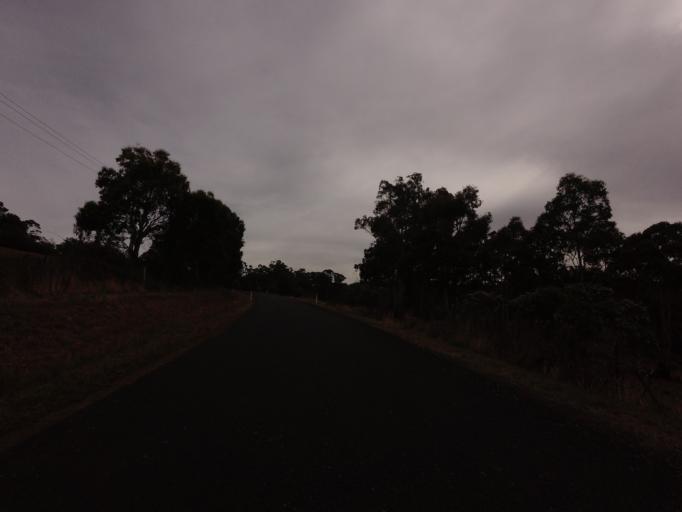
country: AU
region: Tasmania
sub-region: Sorell
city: Sorell
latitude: -42.4752
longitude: 147.5740
